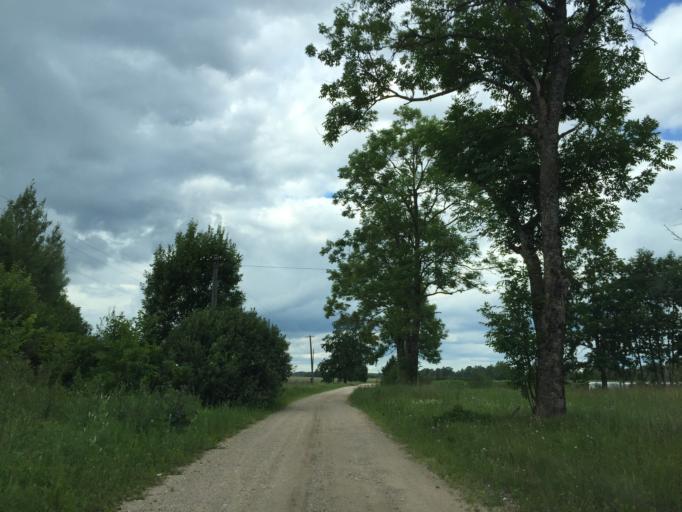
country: LV
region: Ogre
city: Jumprava
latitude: 56.8447
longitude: 25.0511
